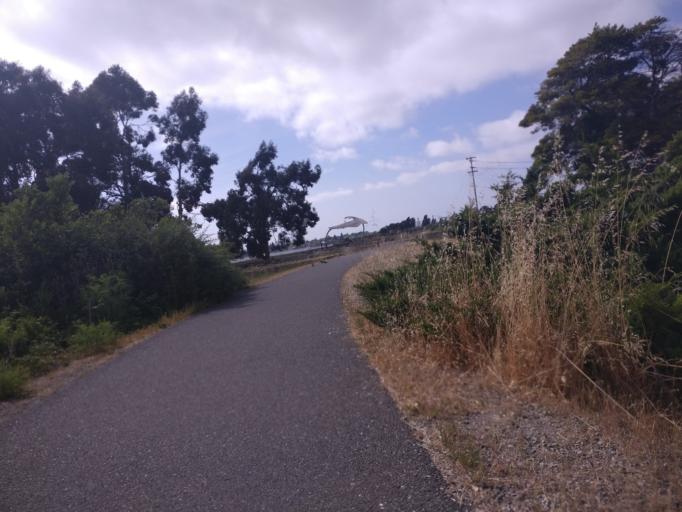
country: US
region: California
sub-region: Alameda County
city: Alameda
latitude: 37.7523
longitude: -122.2103
